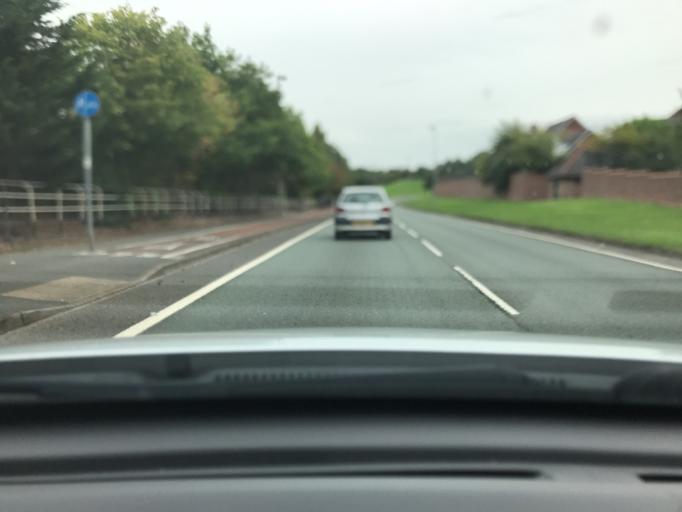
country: GB
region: England
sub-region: Cheshire West and Chester
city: Northwich
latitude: 53.2462
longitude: -2.5170
